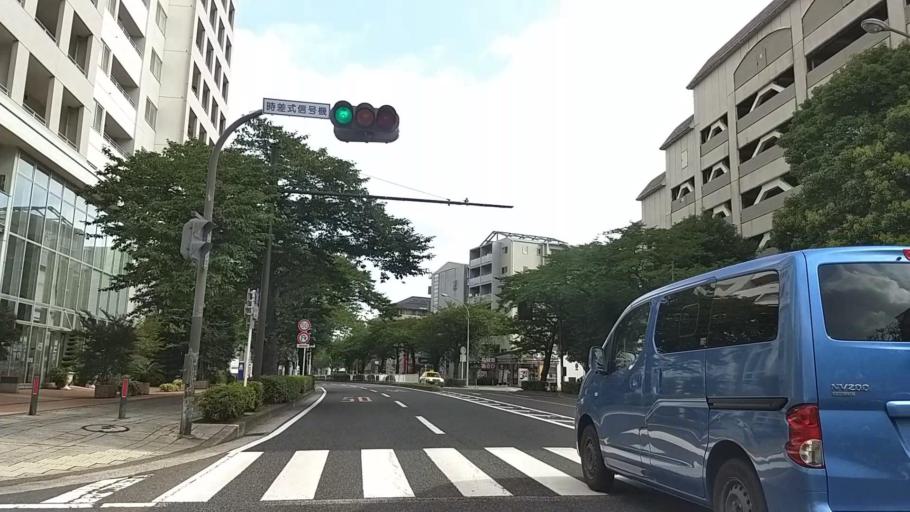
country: JP
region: Kanagawa
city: Yokohama
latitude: 35.4259
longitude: 139.6659
